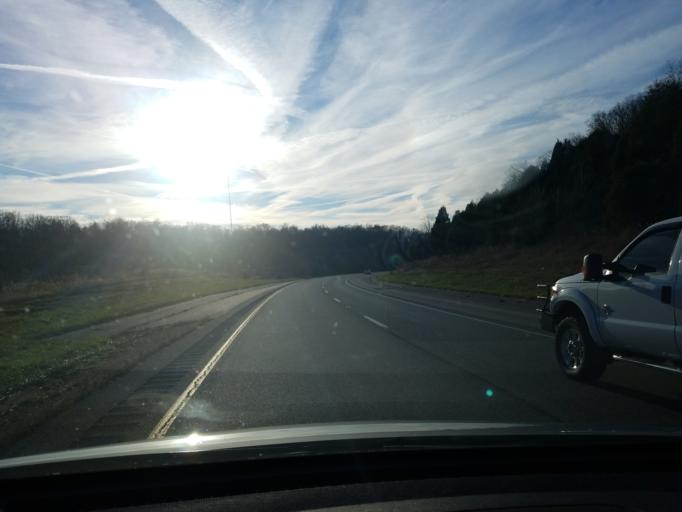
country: US
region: Indiana
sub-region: Crawford County
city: English
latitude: 38.2372
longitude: -86.3724
